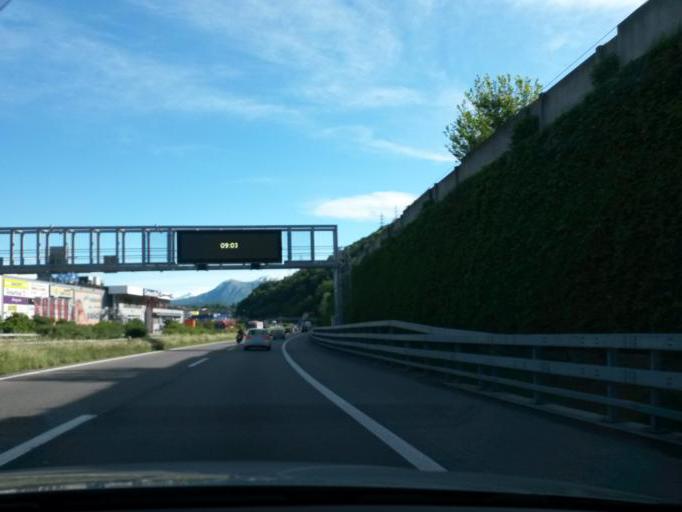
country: CH
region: Ticino
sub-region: Lugano District
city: Montagnola
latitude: 45.9682
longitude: 8.9257
